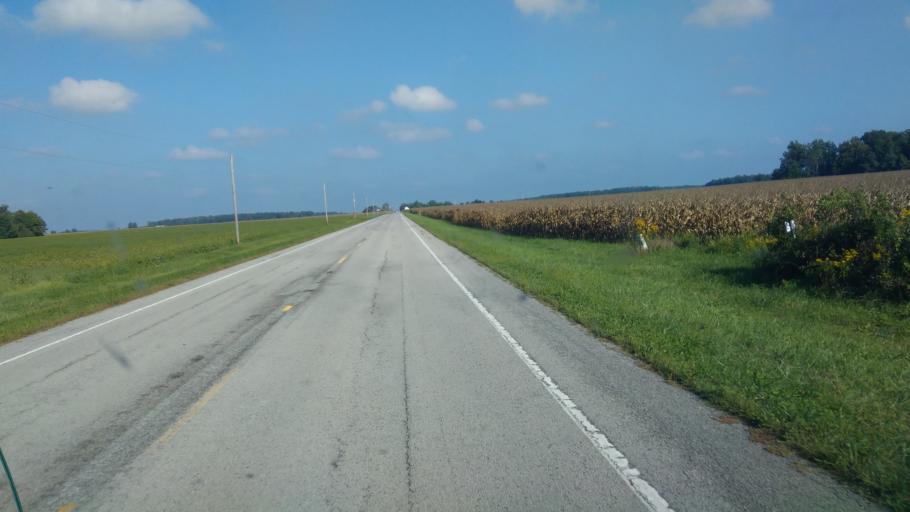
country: US
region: Ohio
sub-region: Hancock County
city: Arlington
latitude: 40.8339
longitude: -83.6240
